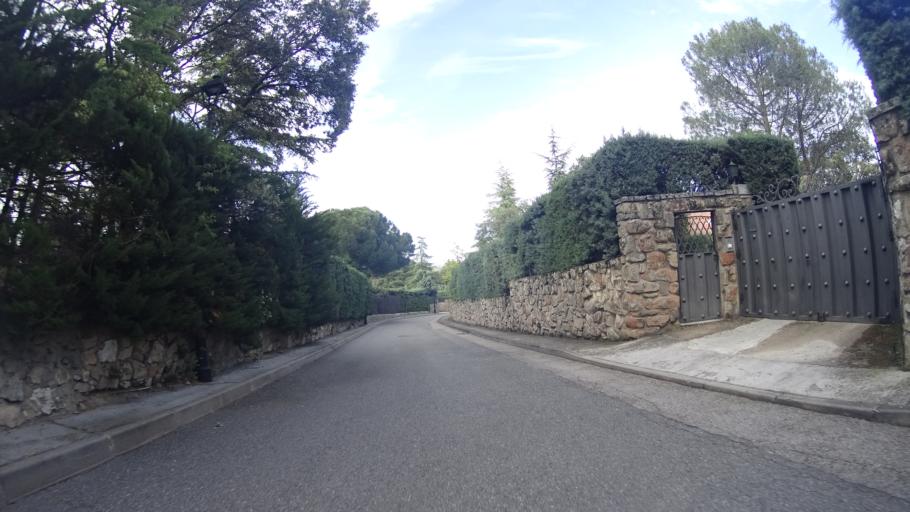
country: ES
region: Madrid
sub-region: Provincia de Madrid
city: Galapagar
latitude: 40.5844
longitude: -3.9707
